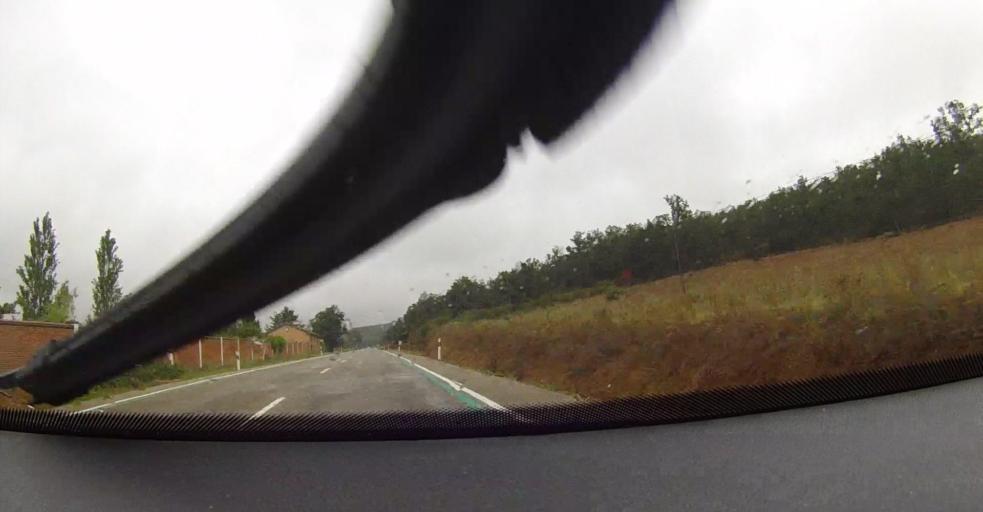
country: ES
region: Castille and Leon
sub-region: Provincia de Palencia
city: Saldana
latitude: 42.5406
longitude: -4.7348
